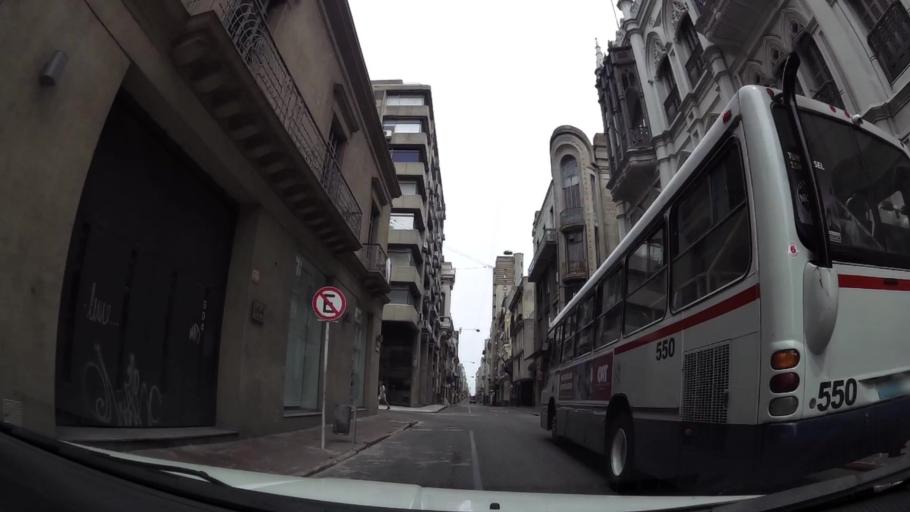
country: UY
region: Montevideo
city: Montevideo
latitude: -34.9051
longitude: -56.2035
